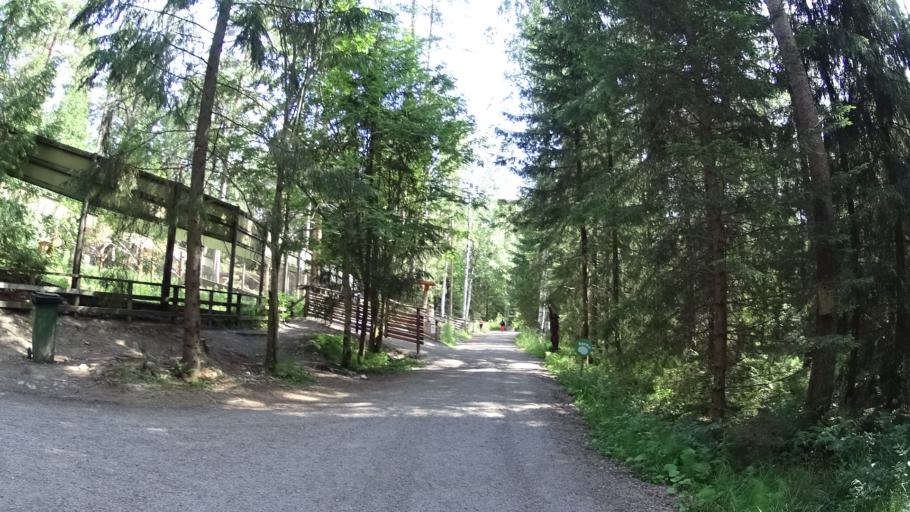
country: FI
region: Southern Ostrobothnia
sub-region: Kuusiokunnat
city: AEhtaeri
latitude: 62.5416
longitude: 24.1777
